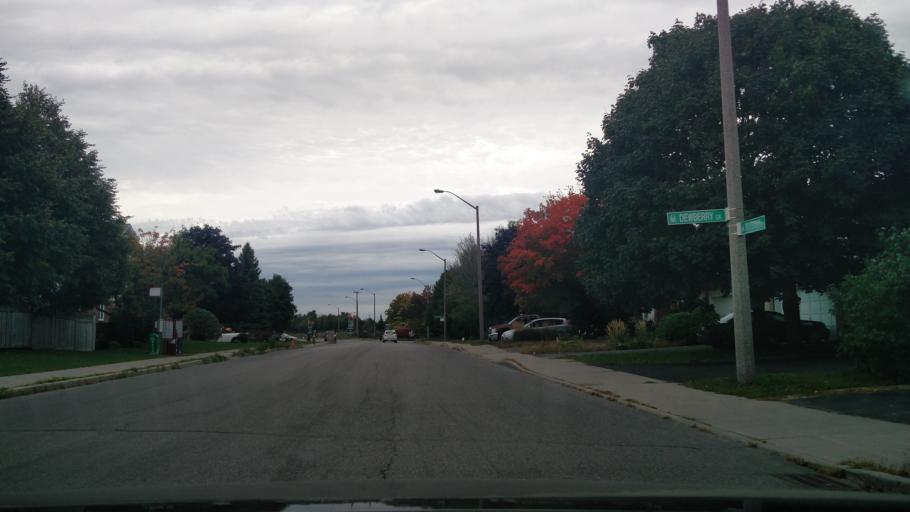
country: CA
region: Ontario
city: Bells Corners
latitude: 45.2885
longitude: -75.7406
